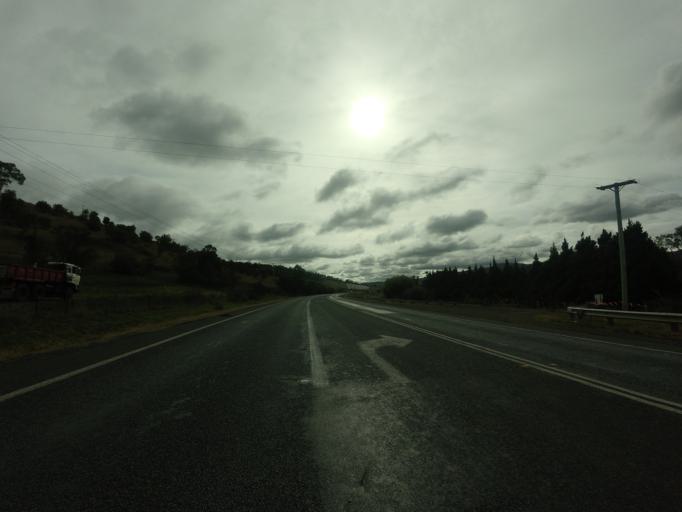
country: AU
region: Tasmania
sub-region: Brighton
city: Bridgewater
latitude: -42.6301
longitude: 147.2227
